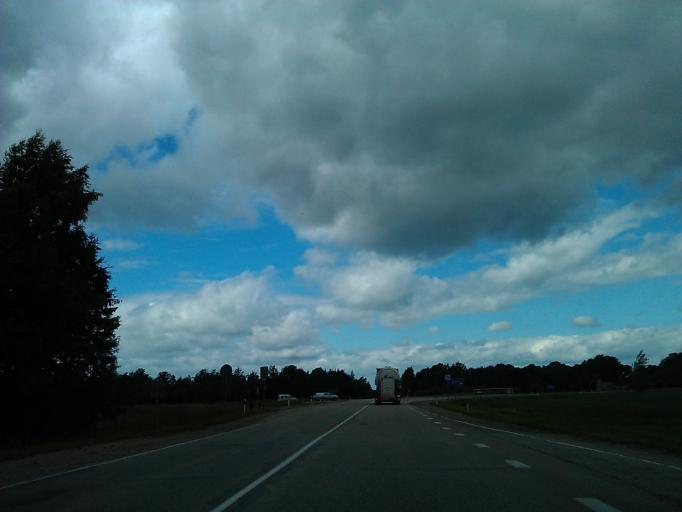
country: LV
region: Tukuma Rajons
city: Tukums
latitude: 56.9326
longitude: 23.2023
